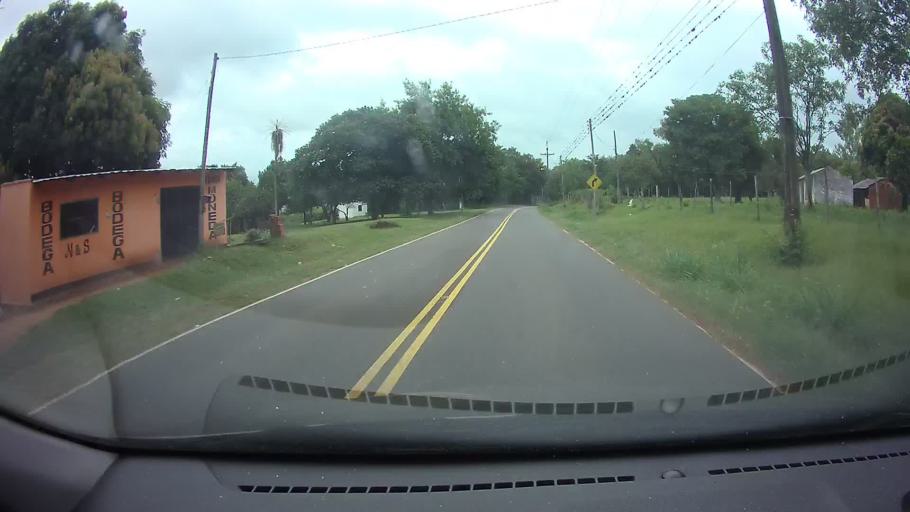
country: PY
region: Central
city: Nueva Italia
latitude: -25.6085
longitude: -57.4206
